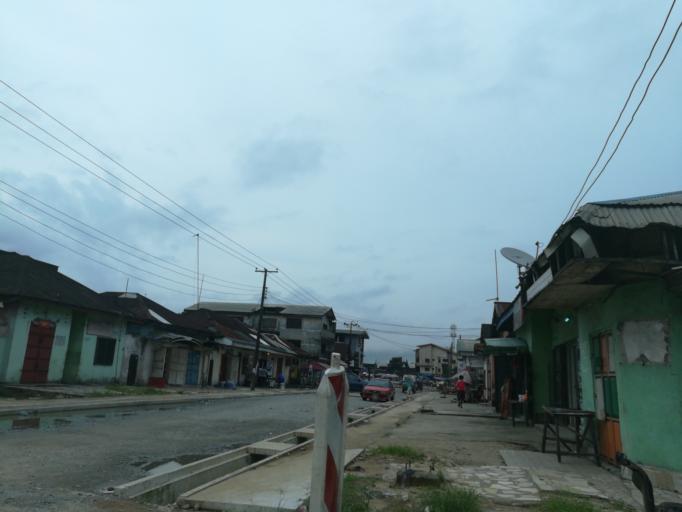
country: NG
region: Rivers
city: Port Harcourt
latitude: 4.7598
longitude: 7.0329
